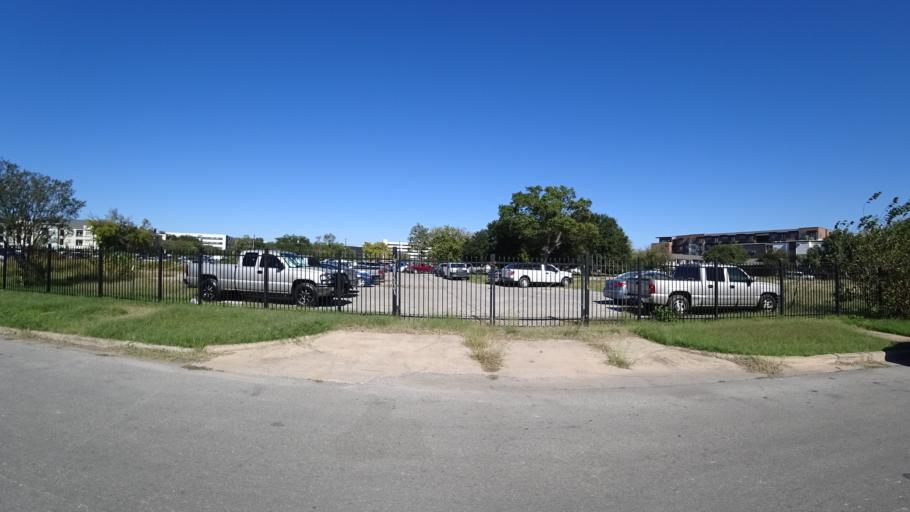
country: US
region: Texas
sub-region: Travis County
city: Austin
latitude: 30.2391
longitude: -97.7233
